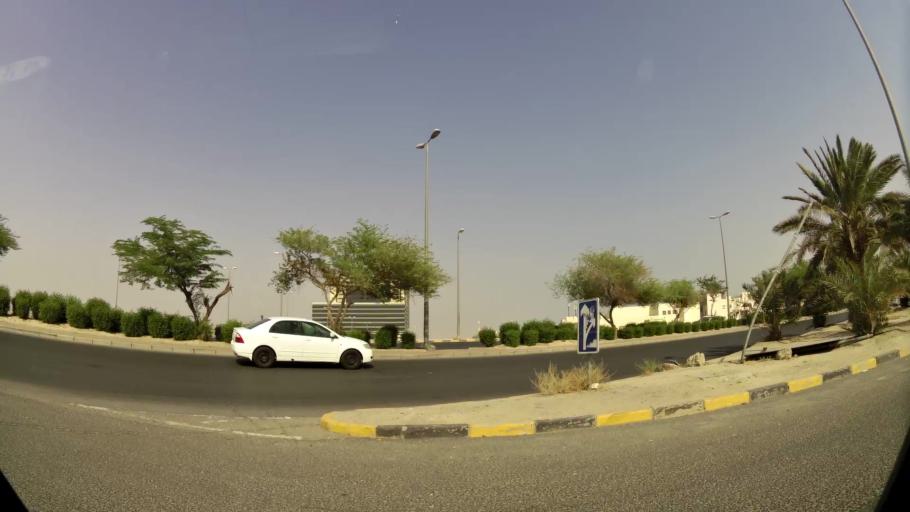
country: KW
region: Muhafazat al Jahra'
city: Al Jahra'
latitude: 29.3494
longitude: 47.6577
